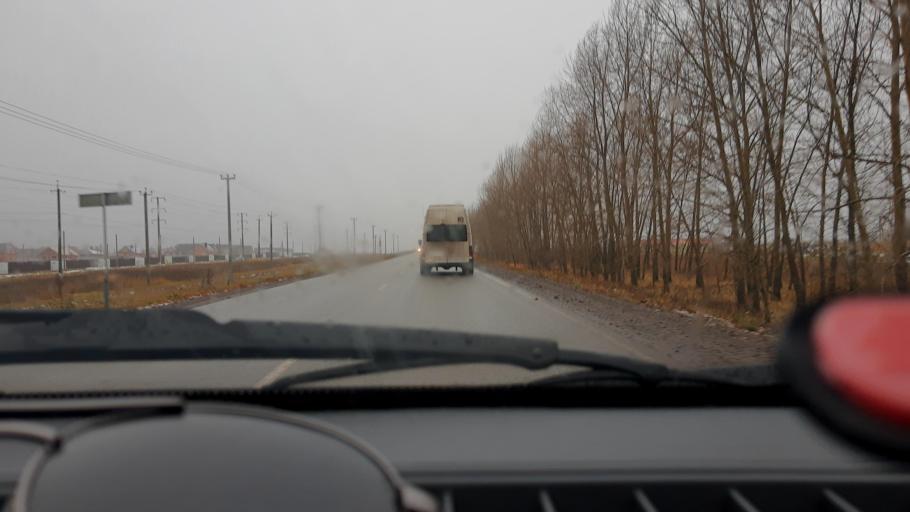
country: RU
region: Bashkortostan
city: Kabakovo
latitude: 54.6138
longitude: 56.1557
